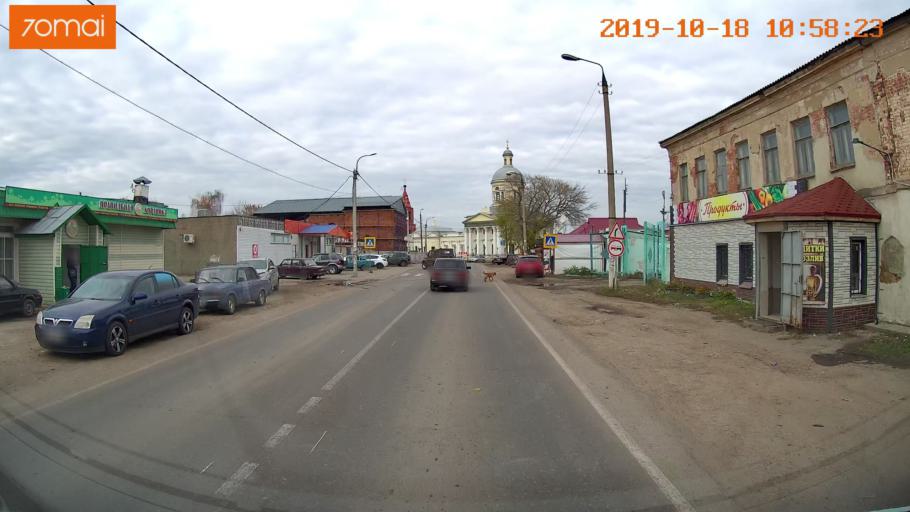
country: RU
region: Tula
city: Yepifan'
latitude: 53.8248
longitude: 38.5548
